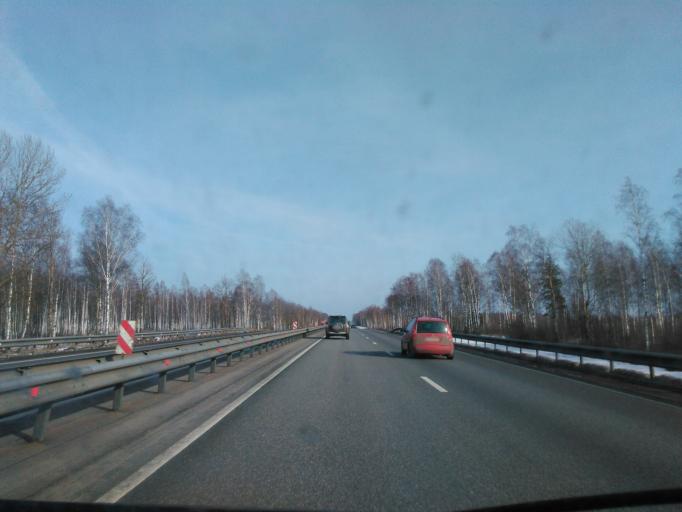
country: RU
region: Smolensk
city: Verkhnedneprovskiy
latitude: 55.1816
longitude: 33.5769
